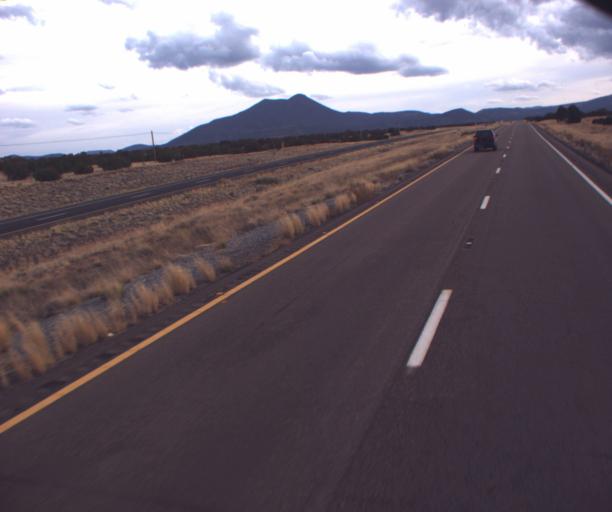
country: US
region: Arizona
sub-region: Coconino County
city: Flagstaff
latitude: 35.4881
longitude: -111.5556
